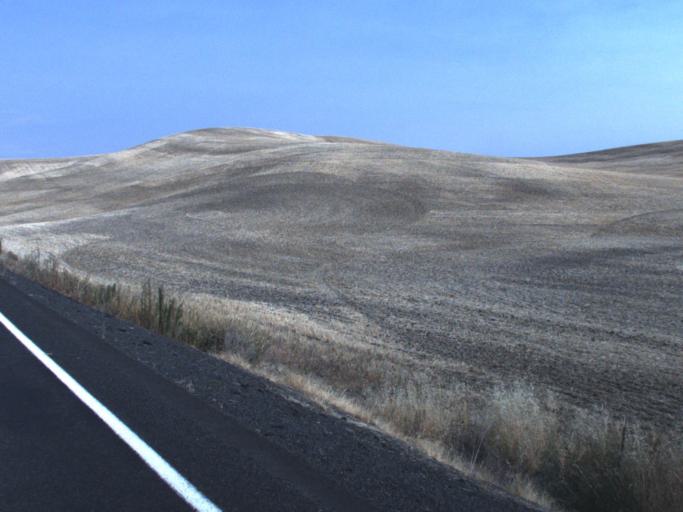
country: US
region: Washington
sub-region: Whitman County
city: Pullman
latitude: 46.9439
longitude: -117.0973
